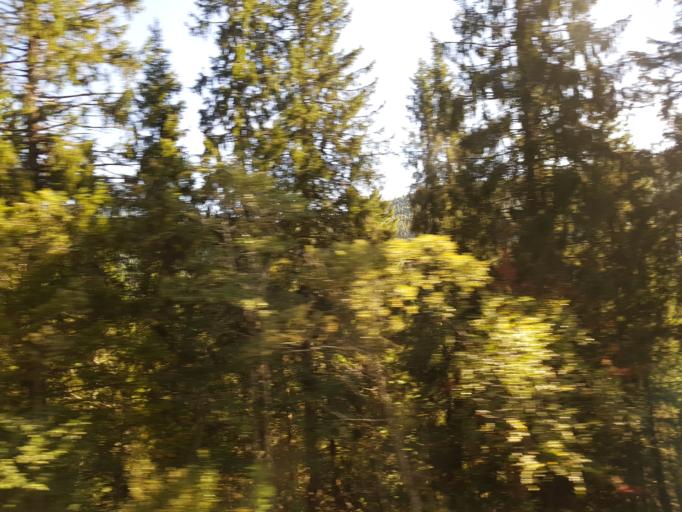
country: NO
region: Sor-Trondelag
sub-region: Rissa
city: Rissa
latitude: 63.6776
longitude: 10.2230
